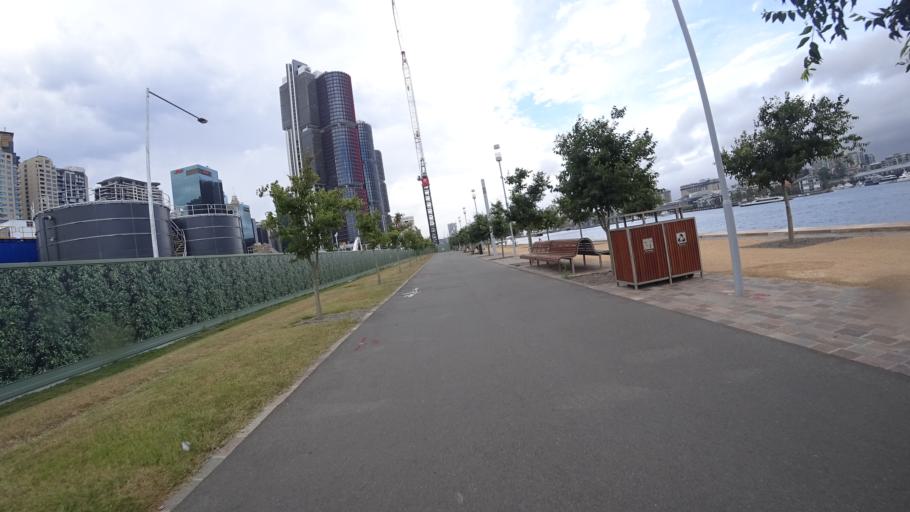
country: AU
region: New South Wales
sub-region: Leichhardt
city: Balmain East
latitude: -33.8605
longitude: 151.2006
